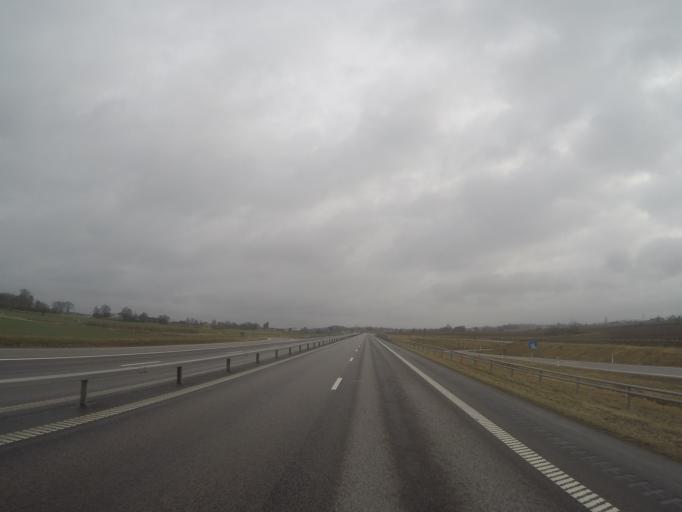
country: SE
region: Skane
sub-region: Hoors Kommun
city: Loberod
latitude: 55.8234
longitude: 13.5228
